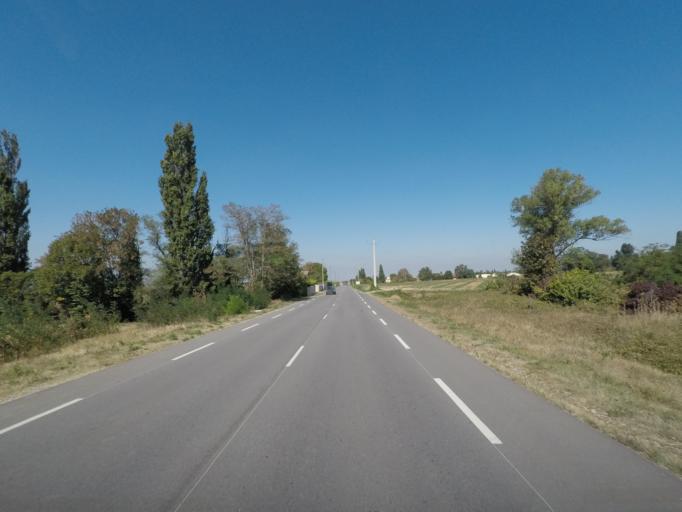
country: FR
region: Rhone-Alpes
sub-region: Departement de la Drome
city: Upie
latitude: 44.7956
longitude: 5.0188
